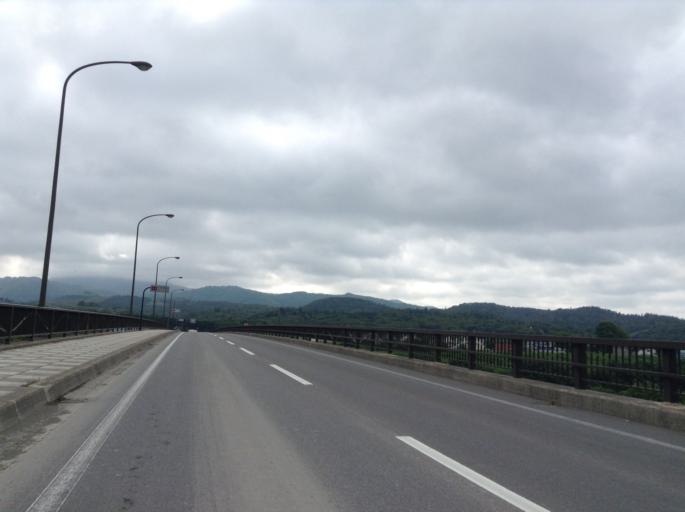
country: JP
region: Hokkaido
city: Makubetsu
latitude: 44.8185
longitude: 142.0682
